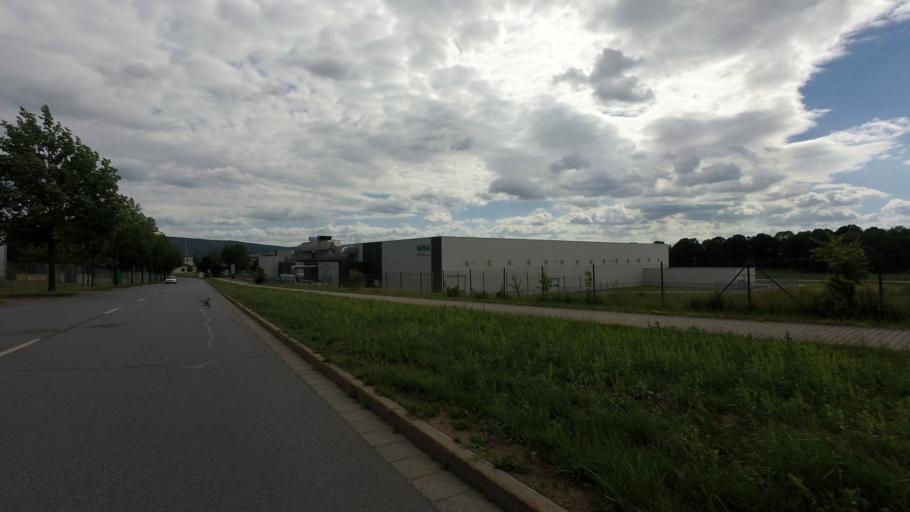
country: DE
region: Saxony
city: Neustadt in Sachsen
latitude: 51.0315
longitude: 14.2301
